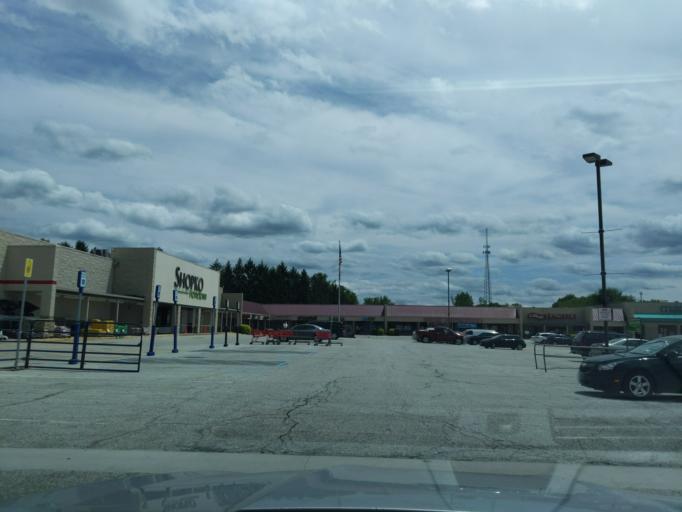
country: US
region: Indiana
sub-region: Ripley County
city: Batesville
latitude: 39.3093
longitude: -85.2144
